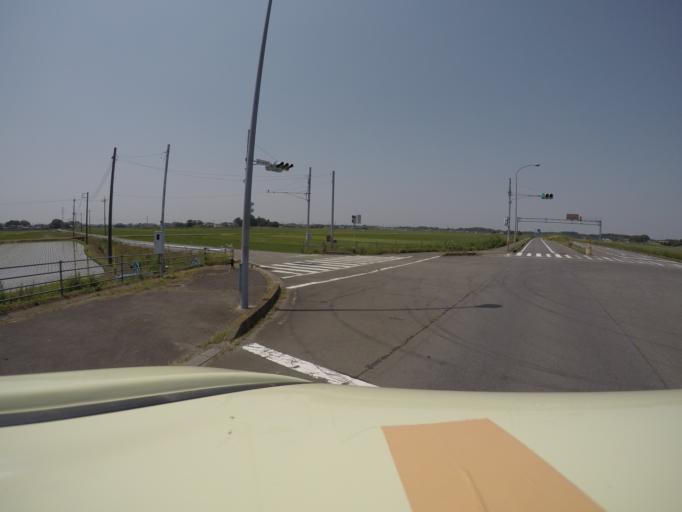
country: JP
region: Ibaraki
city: Mitsukaido
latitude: 36.0387
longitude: 139.9660
